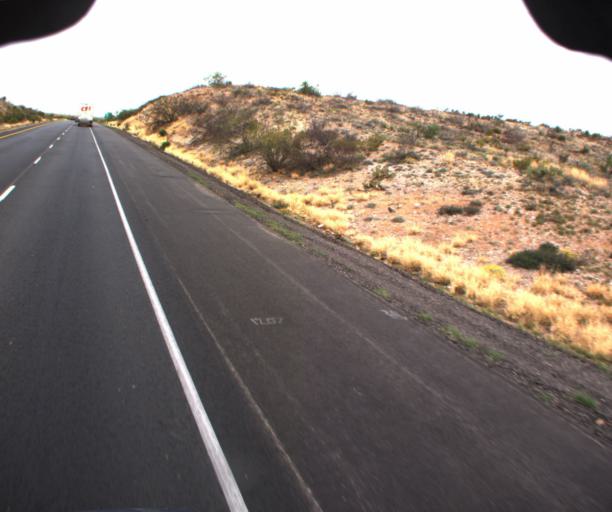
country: US
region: Arizona
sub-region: Pima County
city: Vail
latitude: 31.9977
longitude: -110.6602
